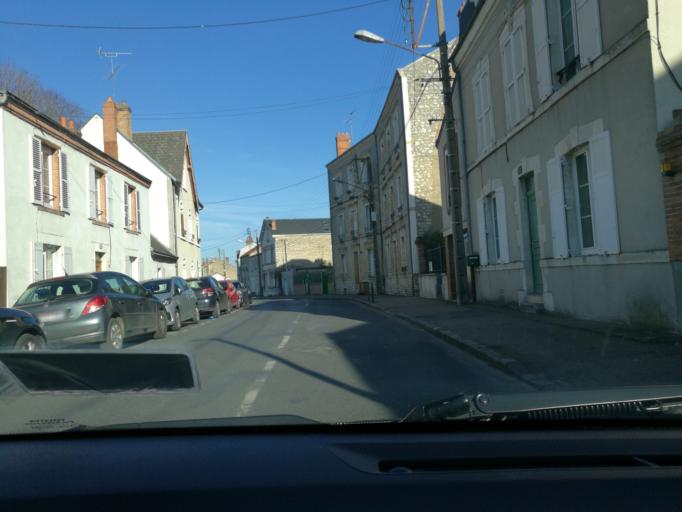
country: FR
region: Centre
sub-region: Departement du Loiret
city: Orleans
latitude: 47.9141
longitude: 1.8942
